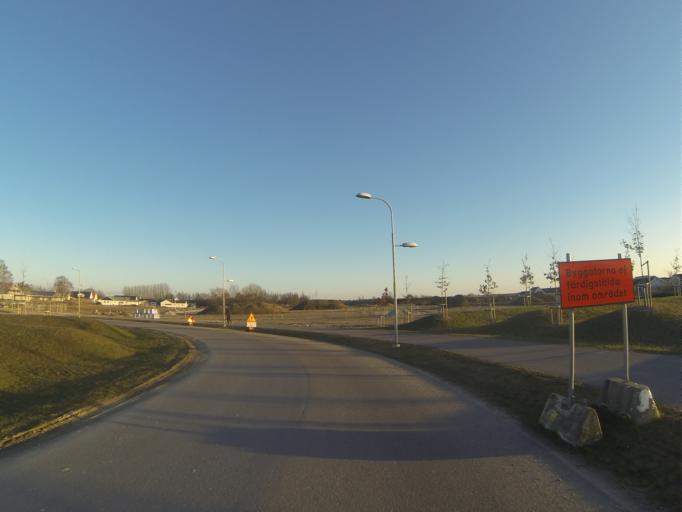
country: SE
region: Skane
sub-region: Staffanstorps Kommun
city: Staffanstorp
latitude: 55.6314
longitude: 13.1967
